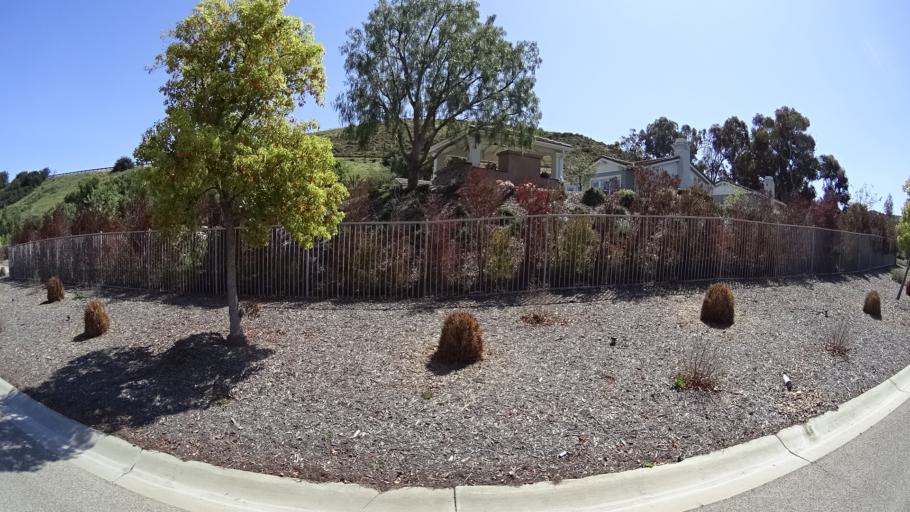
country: US
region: California
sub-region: Ventura County
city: Moorpark
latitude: 34.2484
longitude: -118.8414
